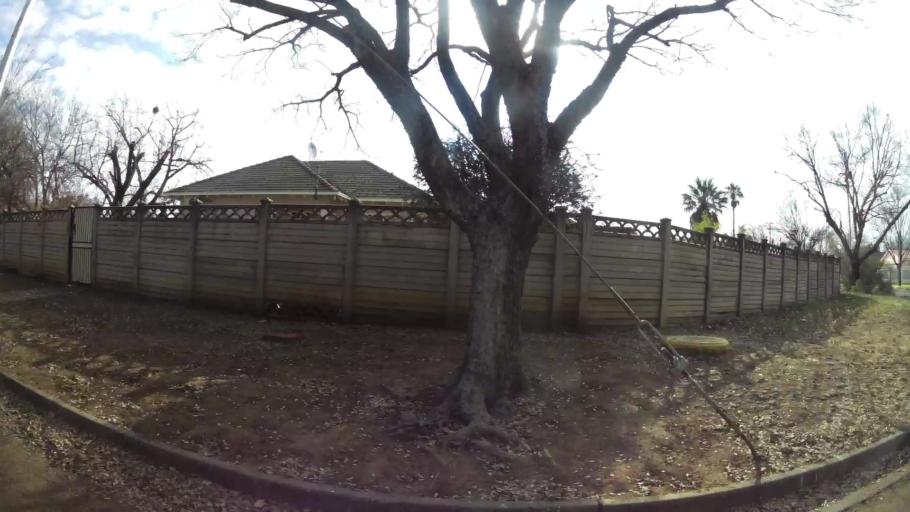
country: ZA
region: Orange Free State
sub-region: Mangaung Metropolitan Municipality
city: Bloemfontein
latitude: -29.0754
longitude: 26.2395
